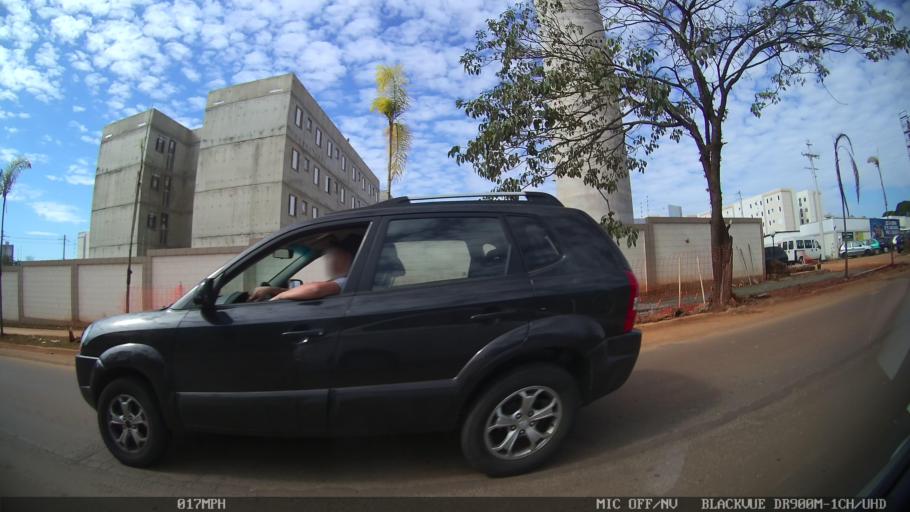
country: BR
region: Sao Paulo
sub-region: Santa Barbara D'Oeste
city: Santa Barbara d'Oeste
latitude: -22.7668
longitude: -47.4041
